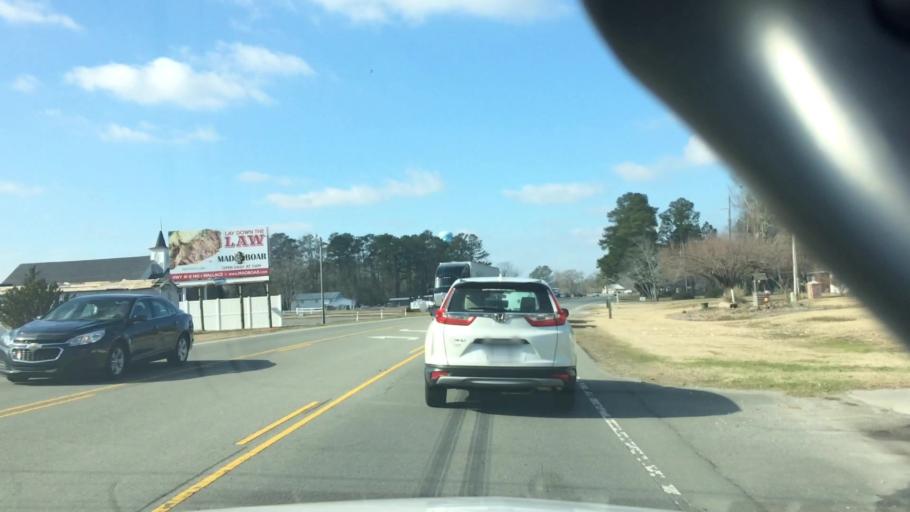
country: US
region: North Carolina
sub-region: Duplin County
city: Beulaville
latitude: 34.8310
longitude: -77.8185
